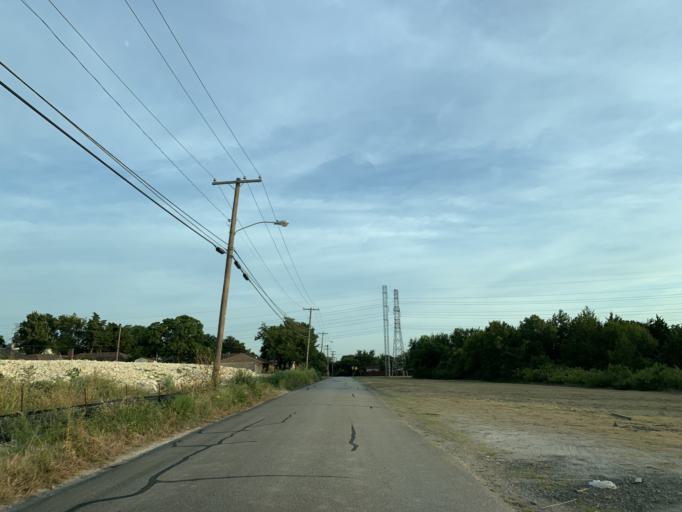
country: US
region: Texas
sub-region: Dallas County
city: Cockrell Hill
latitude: 32.7039
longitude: -96.8829
